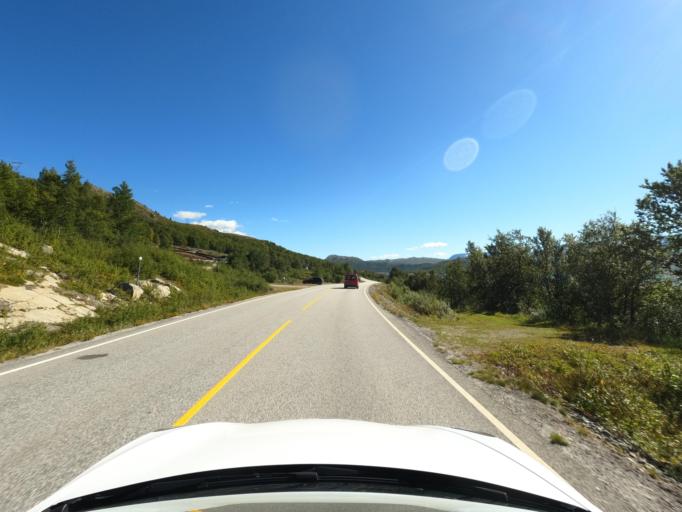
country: NO
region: Buskerud
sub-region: Hol
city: Geilo
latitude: 60.7040
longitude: 7.8657
